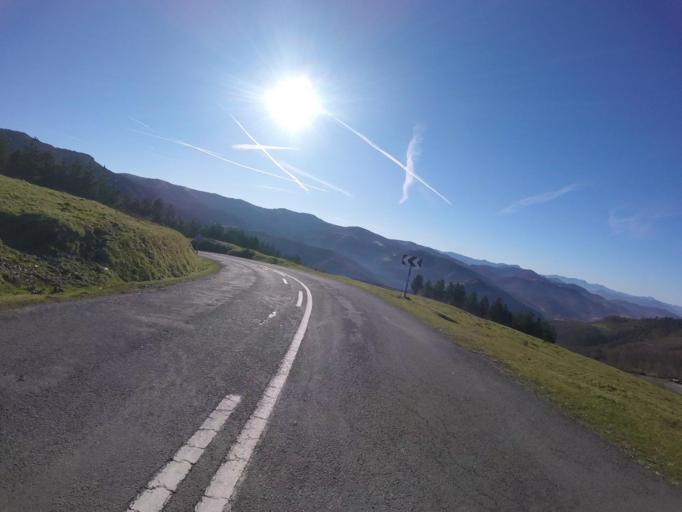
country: ES
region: Basque Country
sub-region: Provincia de Guipuzcoa
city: Irun
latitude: 43.2930
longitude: -1.8077
